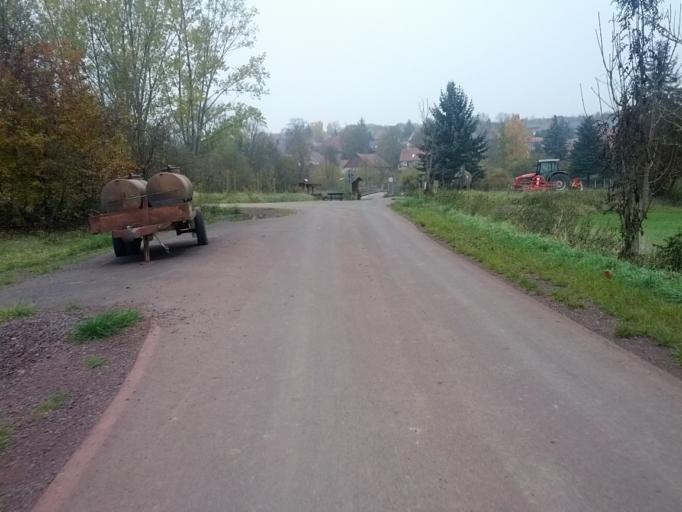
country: DE
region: Thuringia
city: Bischofroda
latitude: 50.9887
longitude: 10.3807
